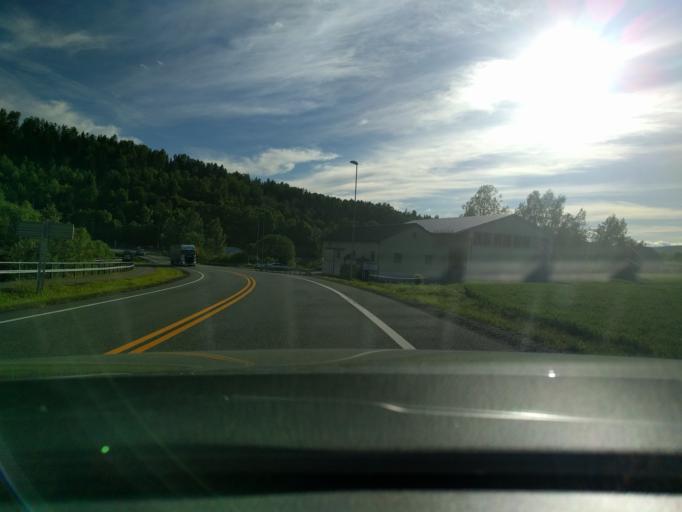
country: NO
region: Vestfold
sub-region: Holmestrand
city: Gullhaug
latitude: 59.5066
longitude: 10.1782
